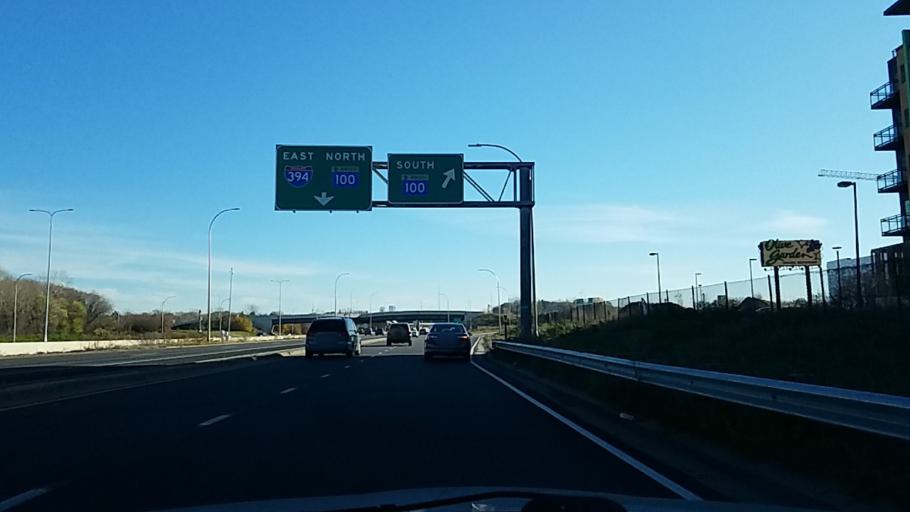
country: US
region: Minnesota
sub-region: Hennepin County
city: Saint Louis Park
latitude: 44.9702
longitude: -93.3471
